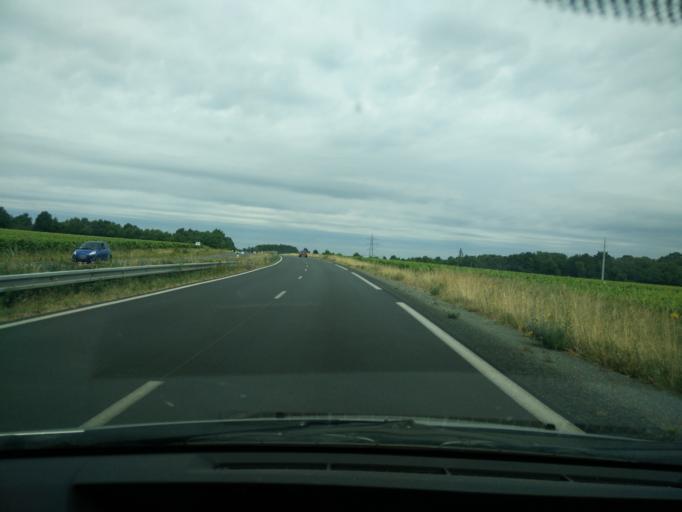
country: FR
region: Pays de la Loire
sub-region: Departement de Maine-et-Loire
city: Juigne-sur-Loire
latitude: 47.3808
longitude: -0.4756
